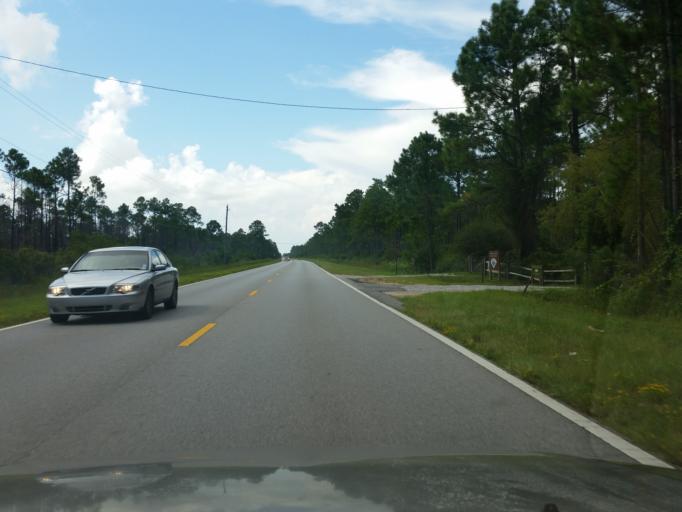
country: US
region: Florida
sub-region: Escambia County
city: Myrtle Grove
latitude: 30.3733
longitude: -87.4023
